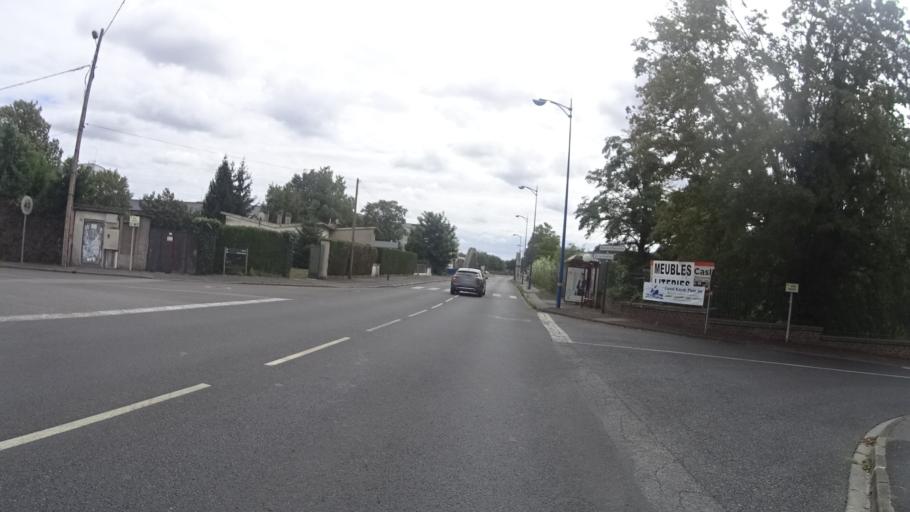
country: FR
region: Picardie
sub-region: Departement de l'Aisne
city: Chauny
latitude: 49.6067
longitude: 3.2228
